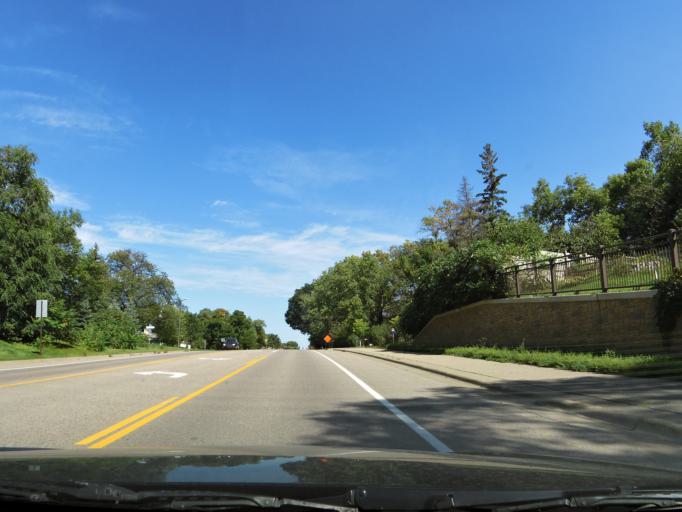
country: US
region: Minnesota
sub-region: Hennepin County
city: Deephaven
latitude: 44.9377
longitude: -93.5024
